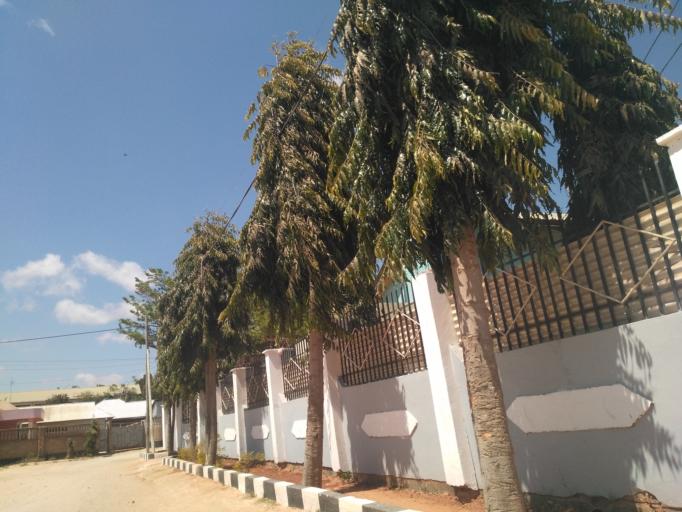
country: TZ
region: Dodoma
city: Kisasa
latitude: -6.1646
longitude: 35.7681
